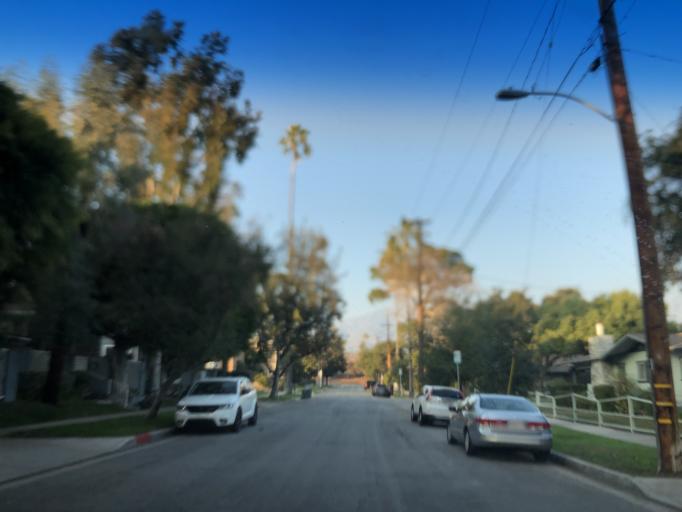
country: US
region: California
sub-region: Los Angeles County
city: Pasadena
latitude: 34.1501
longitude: -118.1230
